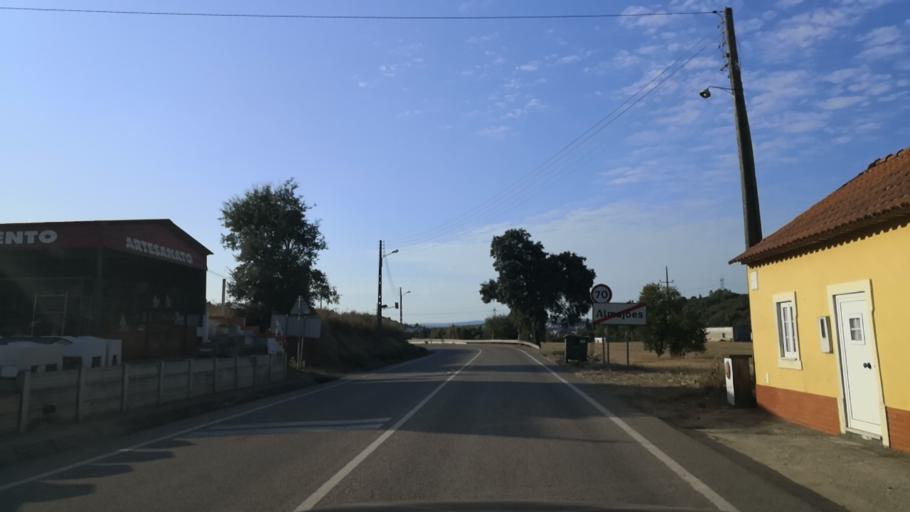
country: PT
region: Santarem
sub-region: Alcanena
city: Alcanena
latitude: 39.3644
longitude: -8.6544
